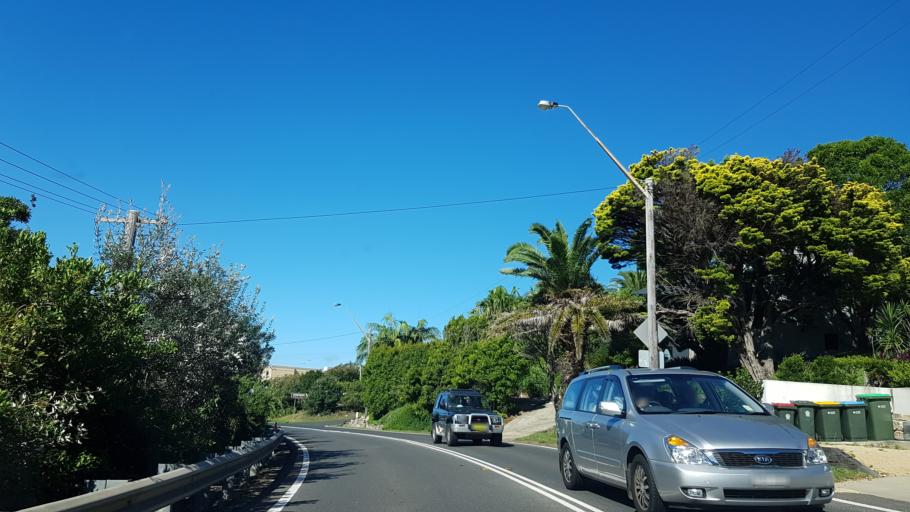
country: AU
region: New South Wales
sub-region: Pittwater
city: Bilgola Beach
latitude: -33.6420
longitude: 151.3312
